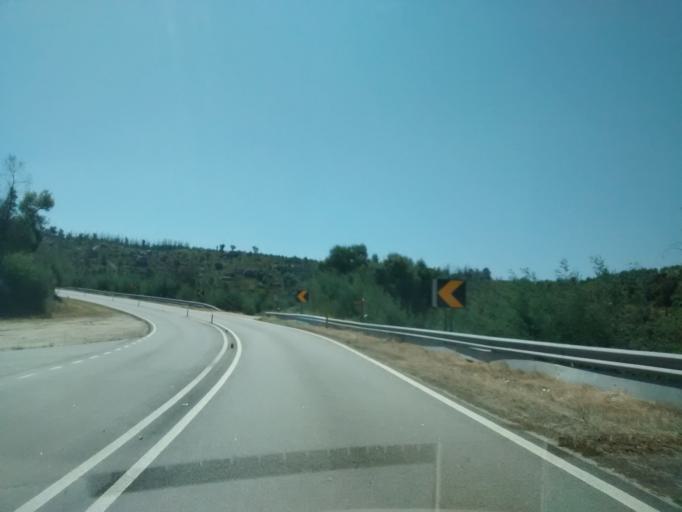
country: PT
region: Coimbra
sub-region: Tabua
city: Tabua
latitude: 40.3700
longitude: -8.0610
